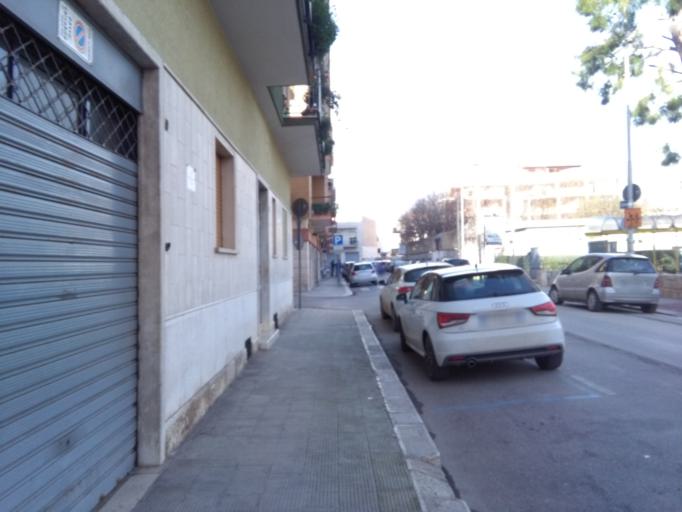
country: IT
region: Apulia
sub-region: Provincia di Barletta - Andria - Trani
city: Andria
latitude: 41.2319
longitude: 16.2965
